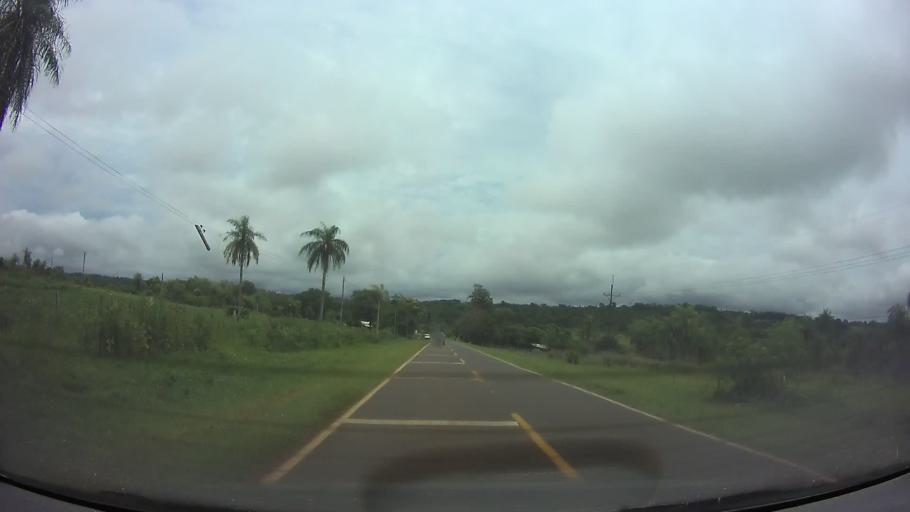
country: PY
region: Paraguari
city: Ybycui
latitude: -25.9751
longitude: -57.0747
